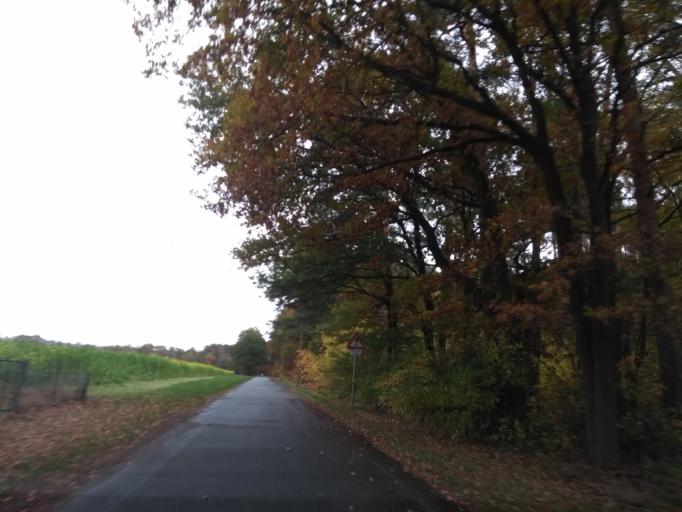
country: DE
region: North Rhine-Westphalia
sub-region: Regierungsbezirk Detmold
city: Hovelhof
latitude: 51.7765
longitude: 8.6824
